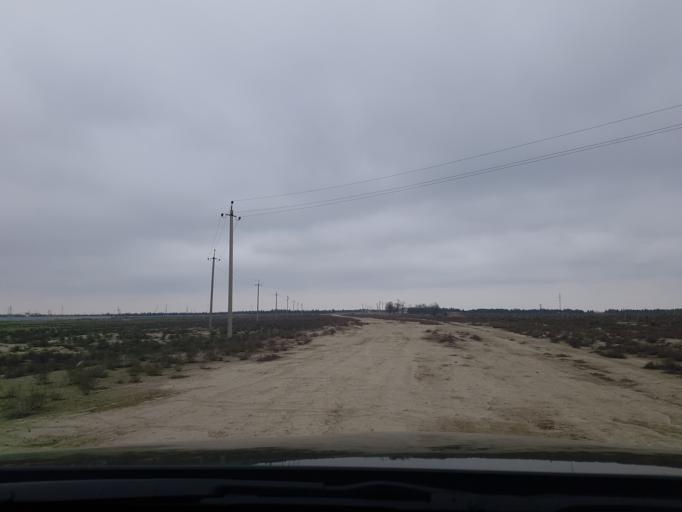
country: TM
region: Ahal
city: Abadan
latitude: 38.1412
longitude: 57.9788
